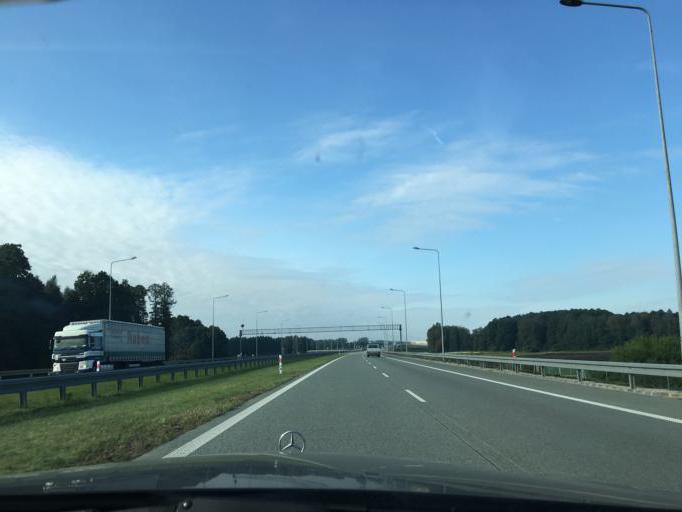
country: PL
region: Lodz Voivodeship
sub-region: Powiat pabianicki
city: Pabianice
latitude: 51.6174
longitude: 19.3752
